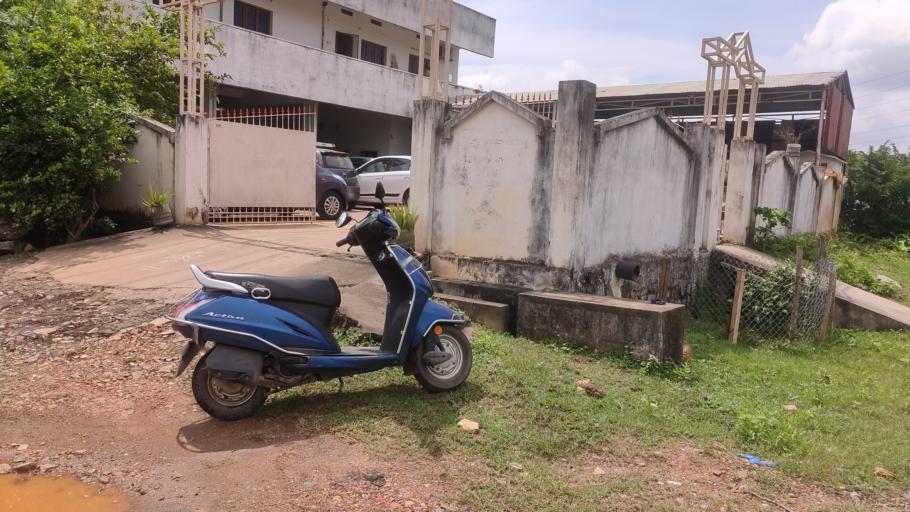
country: IN
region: Telangana
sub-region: Khammam
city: Khammam
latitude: 17.2426
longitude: 80.1938
